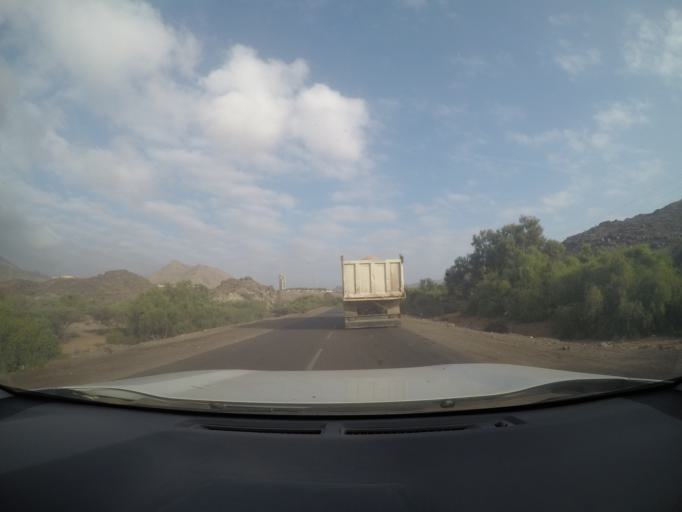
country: YE
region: Lahij
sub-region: Al Milah
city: Al Milah
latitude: 13.3306
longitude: 44.7575
